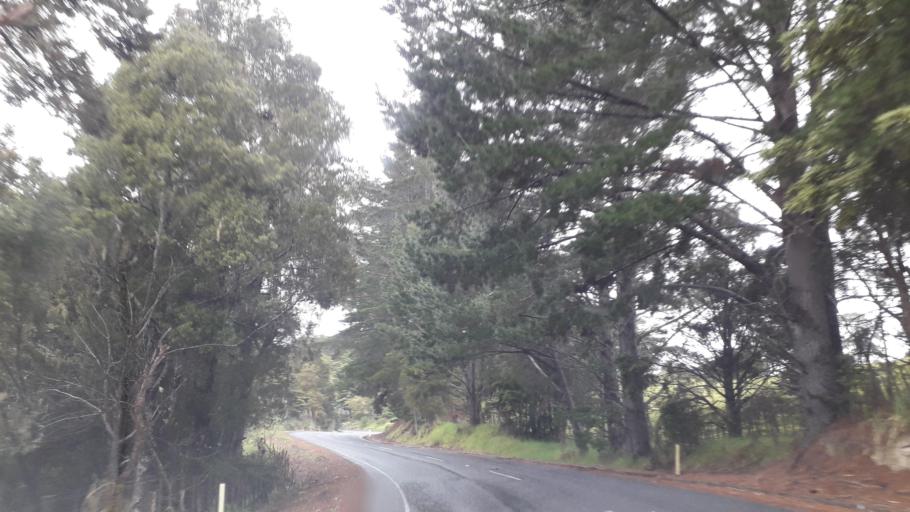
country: NZ
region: Northland
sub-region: Far North District
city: Kaitaia
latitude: -35.3585
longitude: 173.4850
